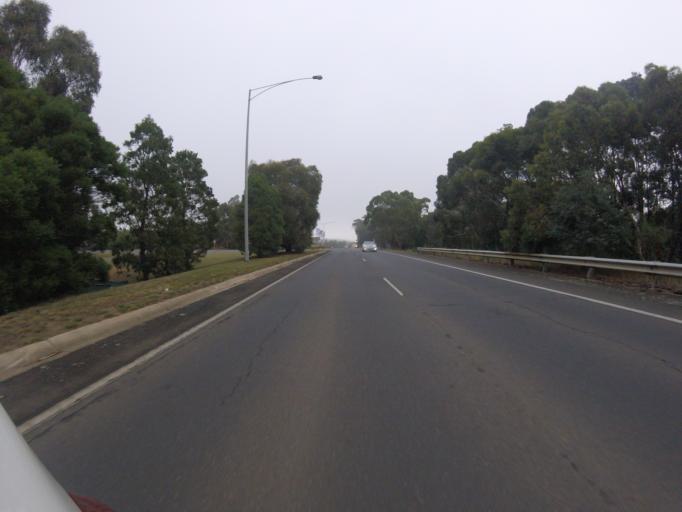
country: AU
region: Victoria
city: Brown Hill
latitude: -37.5593
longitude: 143.9162
